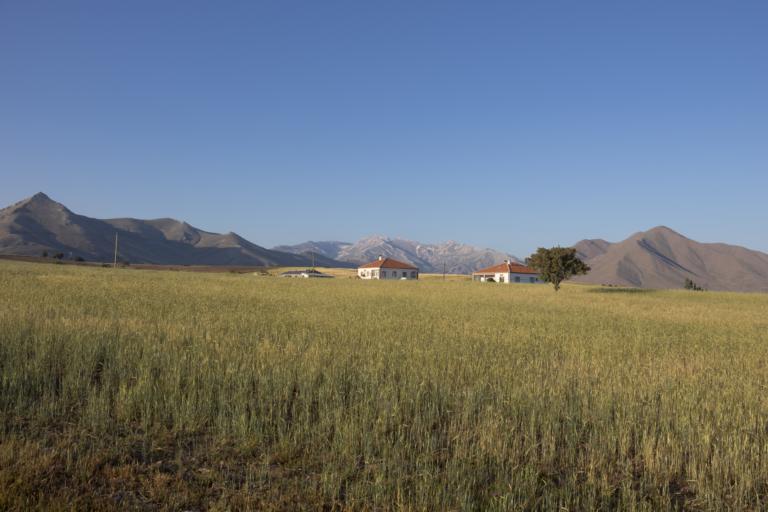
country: TR
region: Adana
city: Tufanbeyli
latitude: 38.3974
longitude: 36.1727
